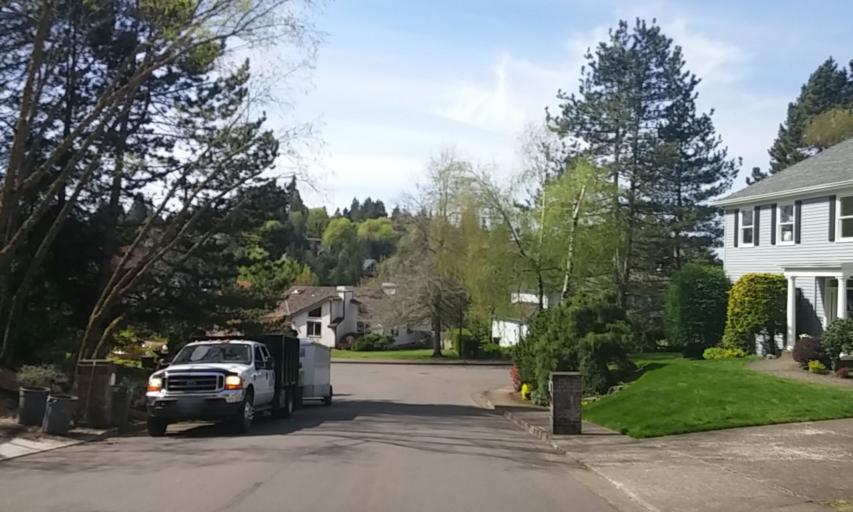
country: US
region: Oregon
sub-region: Washington County
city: West Haven-Sylvan
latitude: 45.5187
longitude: -122.7469
